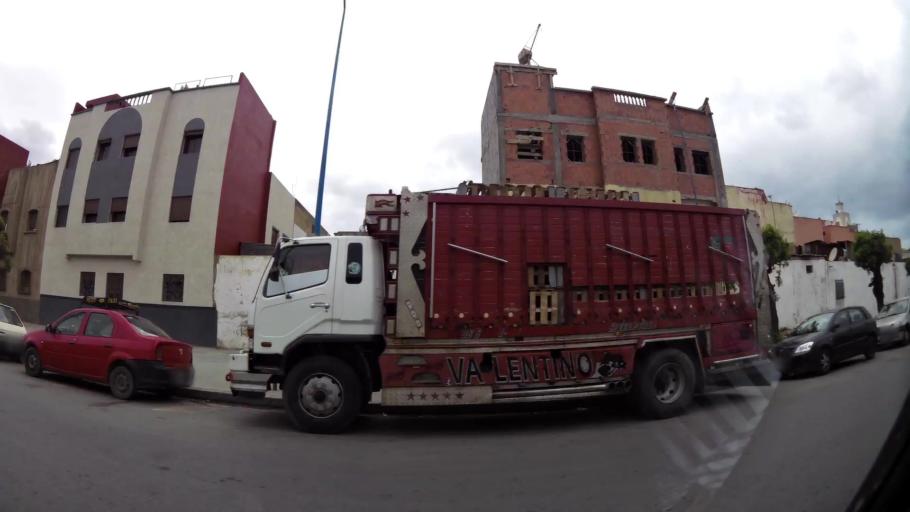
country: MA
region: Grand Casablanca
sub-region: Casablanca
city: Casablanca
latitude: 33.5925
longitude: -7.5691
